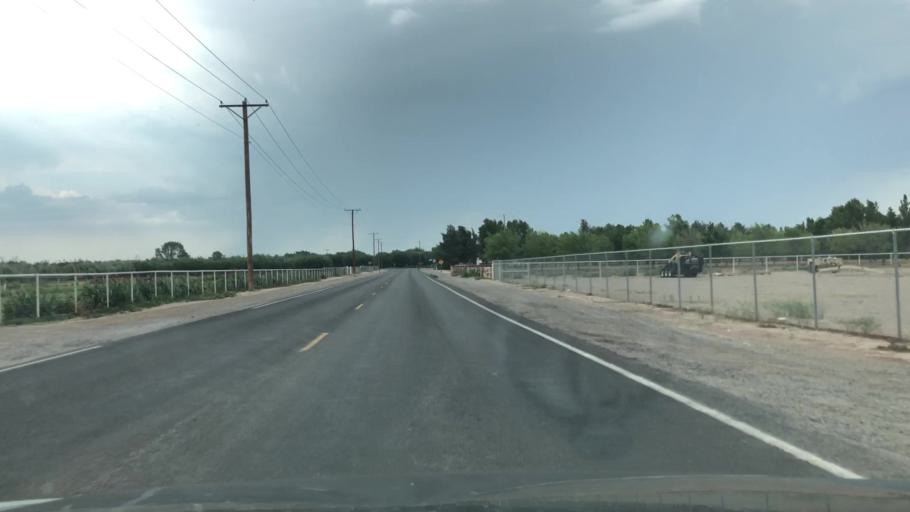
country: US
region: Texas
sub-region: El Paso County
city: Canutillo
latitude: 31.9293
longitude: -106.6290
